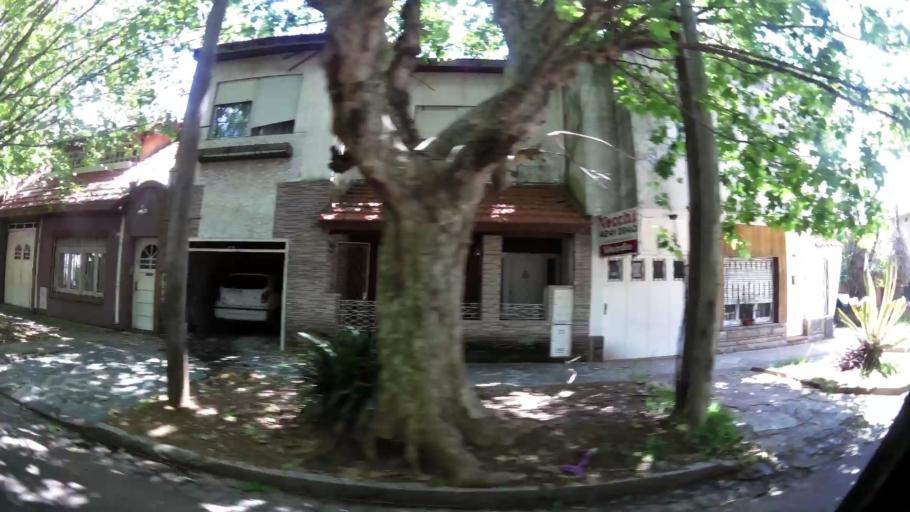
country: AR
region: Buenos Aires
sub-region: Partido de Lomas de Zamora
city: Lomas de Zamora
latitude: -34.7327
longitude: -58.3998
